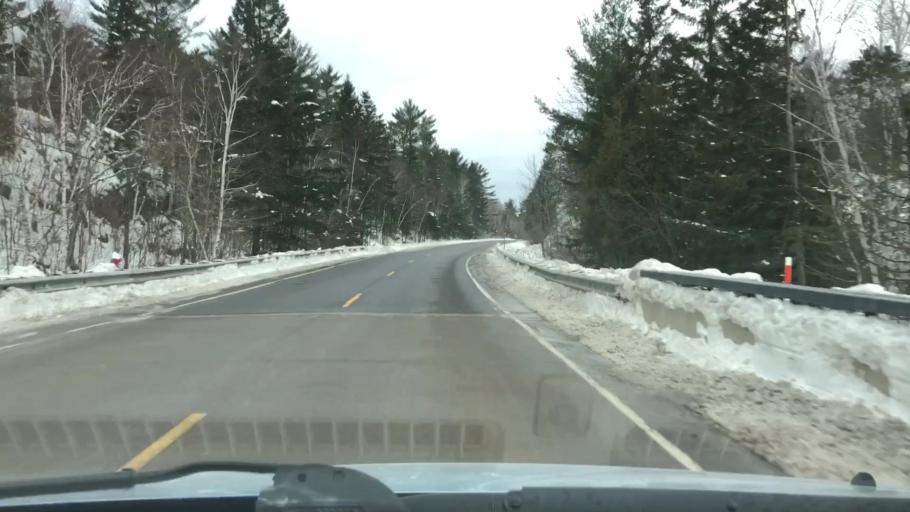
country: US
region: Minnesota
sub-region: Carlton County
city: Carlton
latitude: 46.6648
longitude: -92.4056
